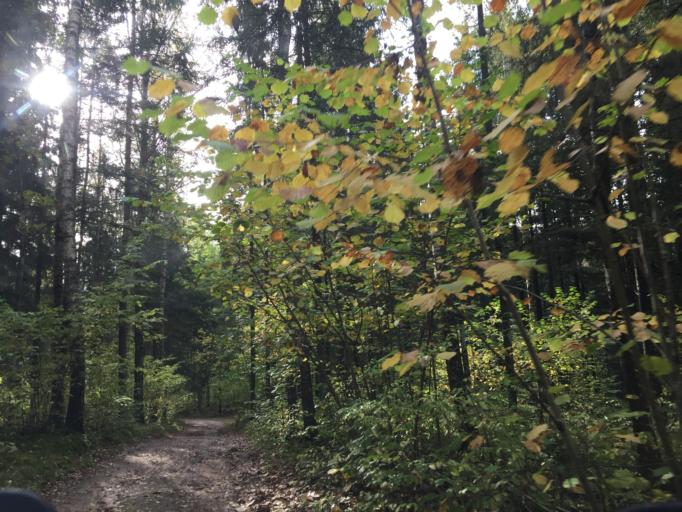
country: LV
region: Jaunpils
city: Jaunpils
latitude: 56.5937
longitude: 23.0124
